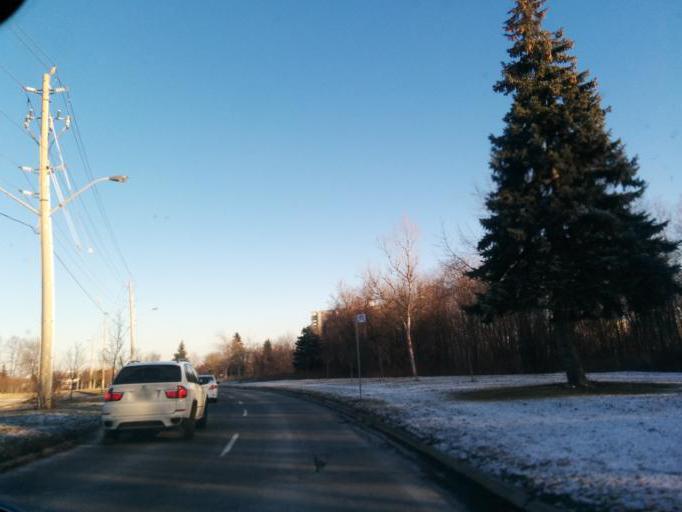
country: CA
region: Ontario
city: Etobicoke
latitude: 43.6457
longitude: -79.5947
